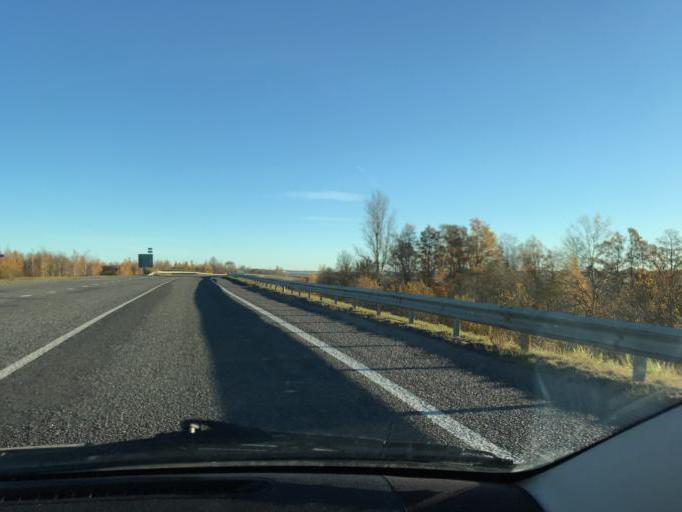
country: BY
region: Vitebsk
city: Vitebsk
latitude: 55.1053
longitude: 30.3029
